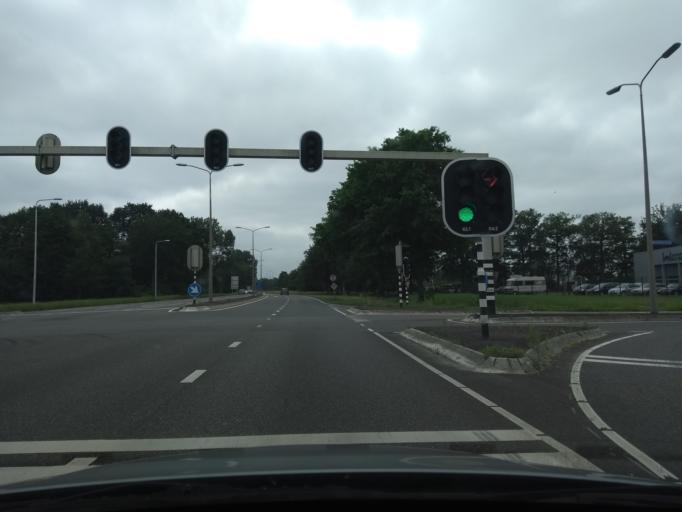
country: NL
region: Overijssel
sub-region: Gemeente Wierden
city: Wierden
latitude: 52.3516
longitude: 6.6244
